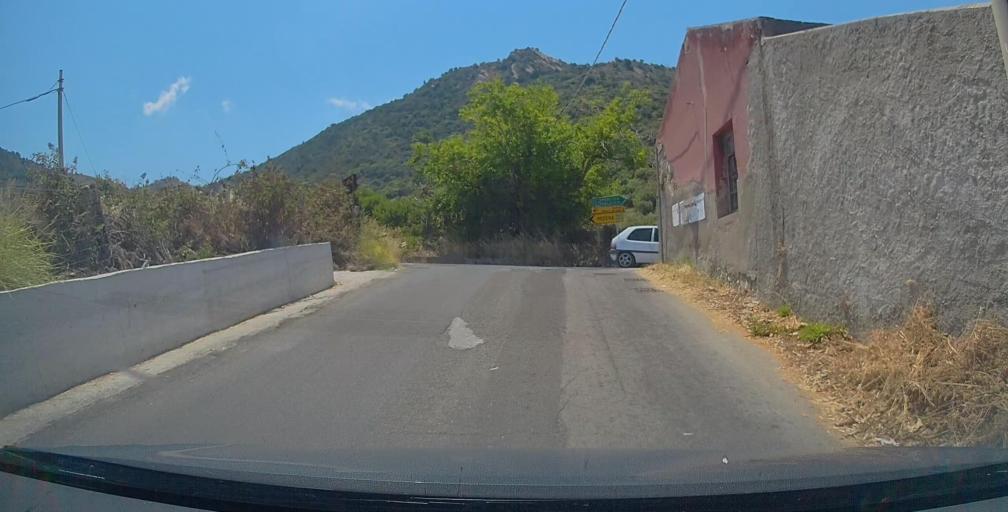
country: IT
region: Sicily
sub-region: Messina
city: Oliveri
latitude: 38.1421
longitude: 15.0155
